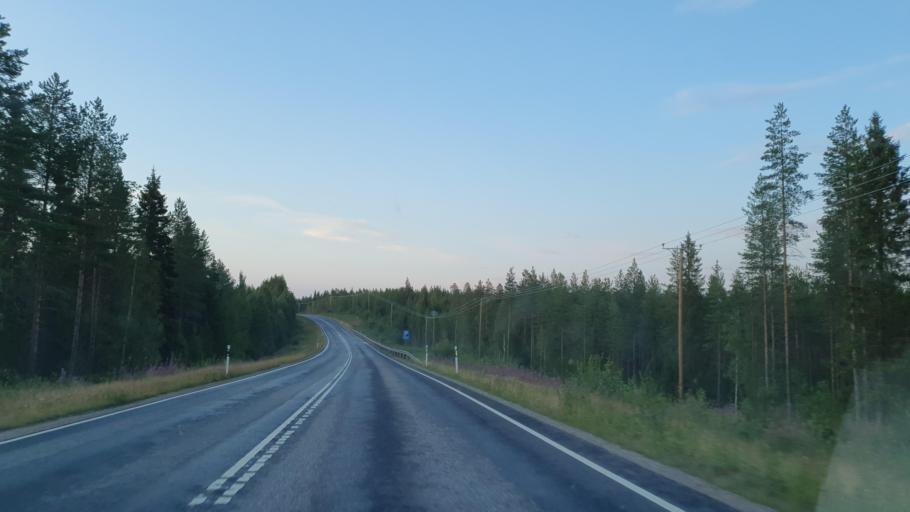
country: FI
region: Kainuu
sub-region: Kehys-Kainuu
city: Hyrynsalmi
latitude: 64.7421
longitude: 28.6792
